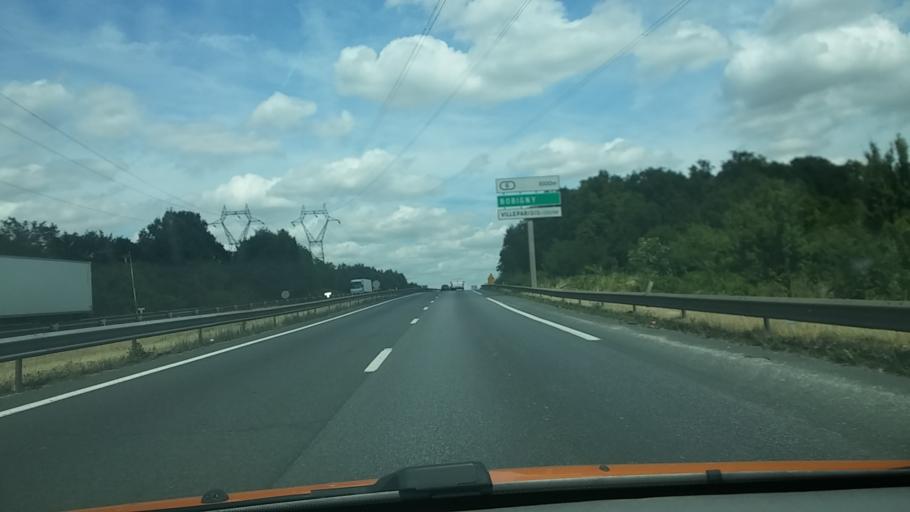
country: FR
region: Ile-de-France
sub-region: Departement de Seine-et-Marne
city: Le Pin
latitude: 48.9251
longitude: 2.6293
